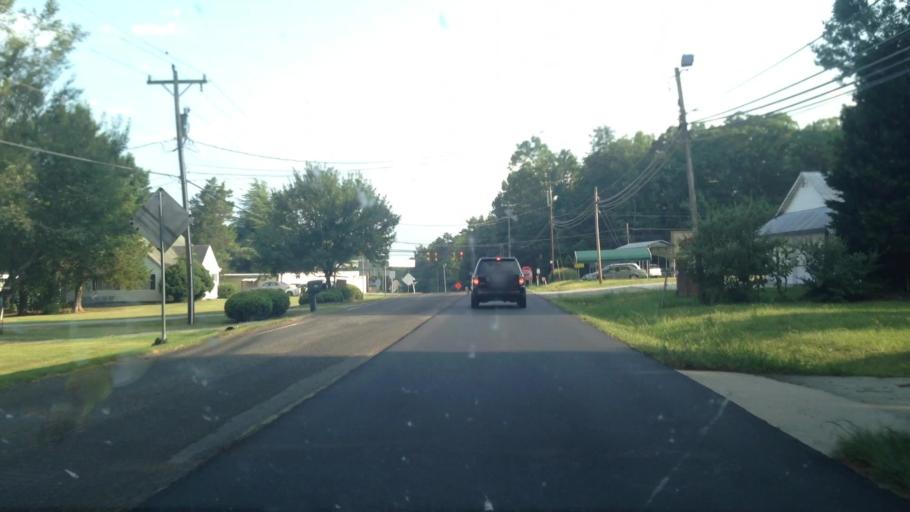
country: US
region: North Carolina
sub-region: Davidson County
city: Wallburg
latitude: 36.0208
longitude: -80.0597
